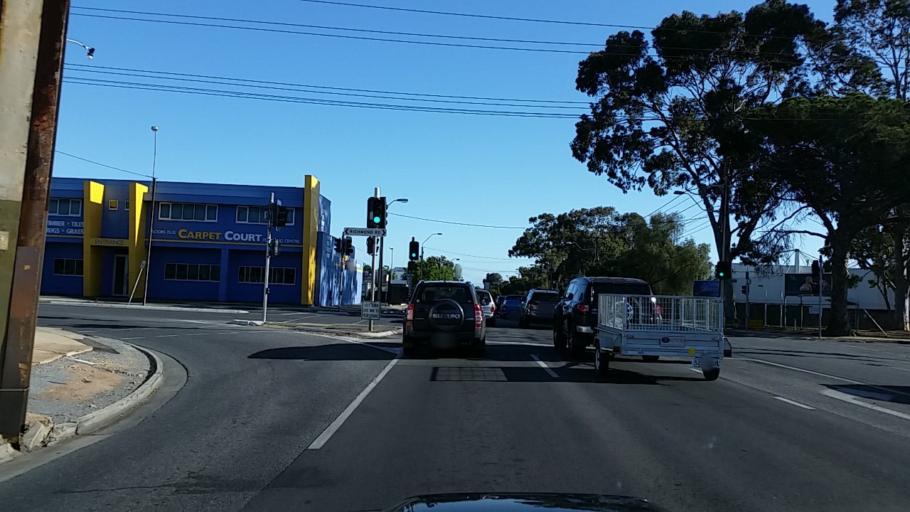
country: AU
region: South Australia
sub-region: City of West Torrens
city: Plympton
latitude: -34.9427
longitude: 138.5533
